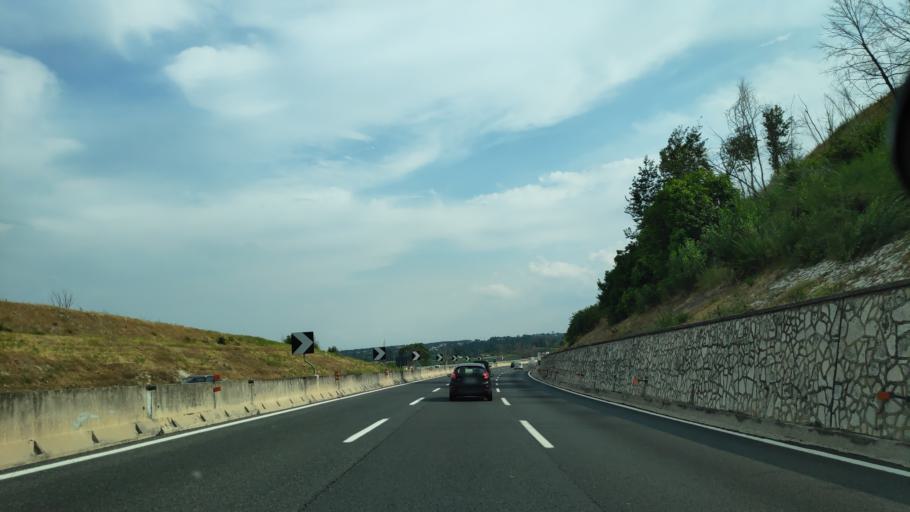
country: IT
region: Latium
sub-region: Citta metropolitana di Roma Capitale
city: Civitella San Paolo
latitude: 42.1964
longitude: 12.6038
